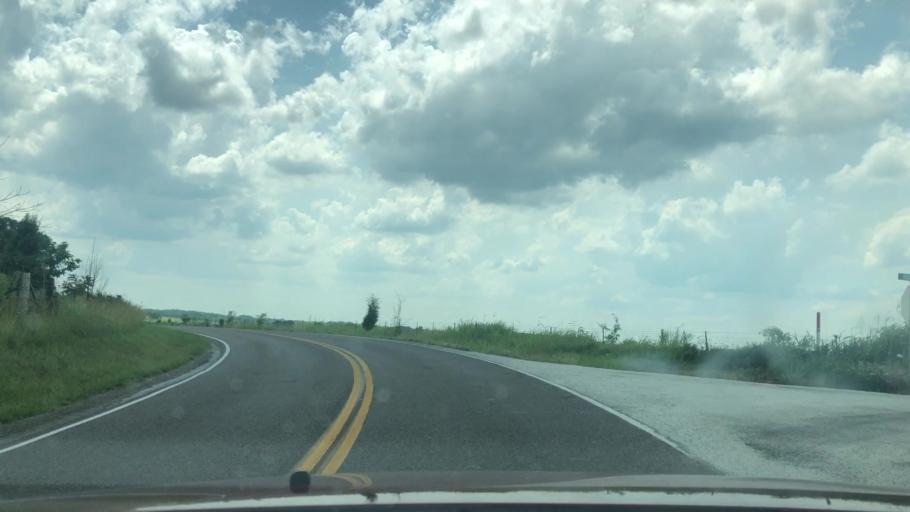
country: US
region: Missouri
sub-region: Christian County
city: Ozark
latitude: 36.9432
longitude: -93.2489
